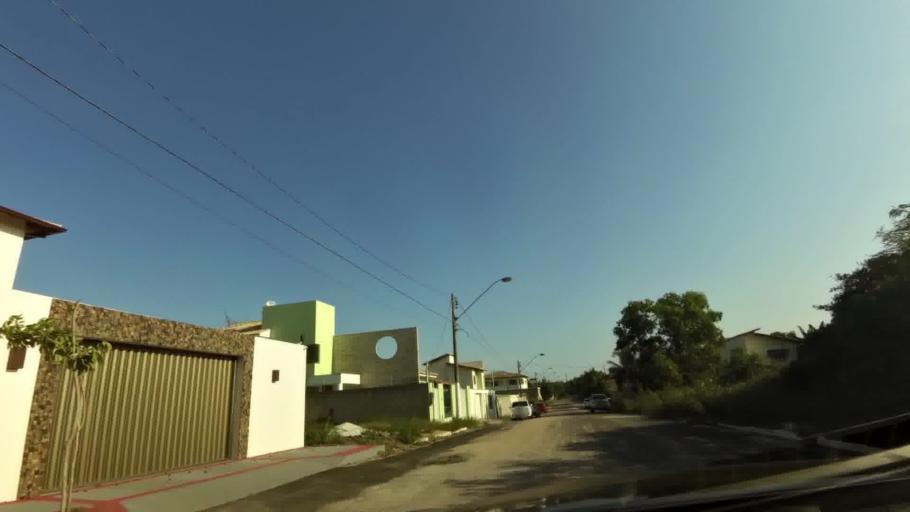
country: BR
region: Espirito Santo
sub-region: Vila Velha
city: Vila Velha
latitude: -20.4738
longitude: -40.3474
